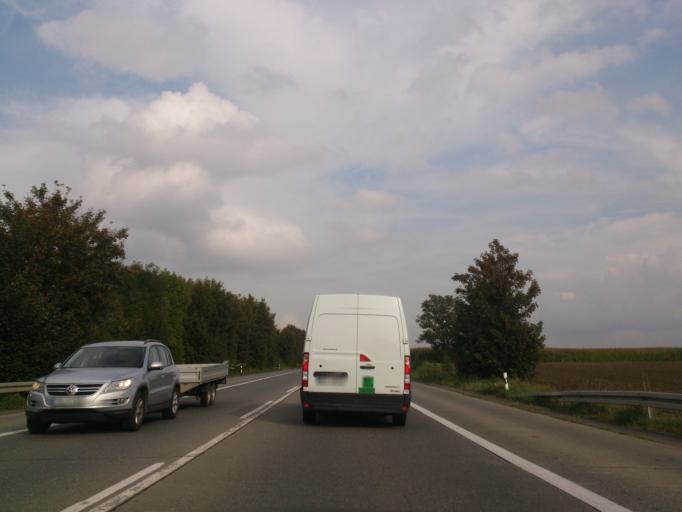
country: DE
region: North Rhine-Westphalia
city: Geseke
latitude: 51.6357
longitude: 8.4858
